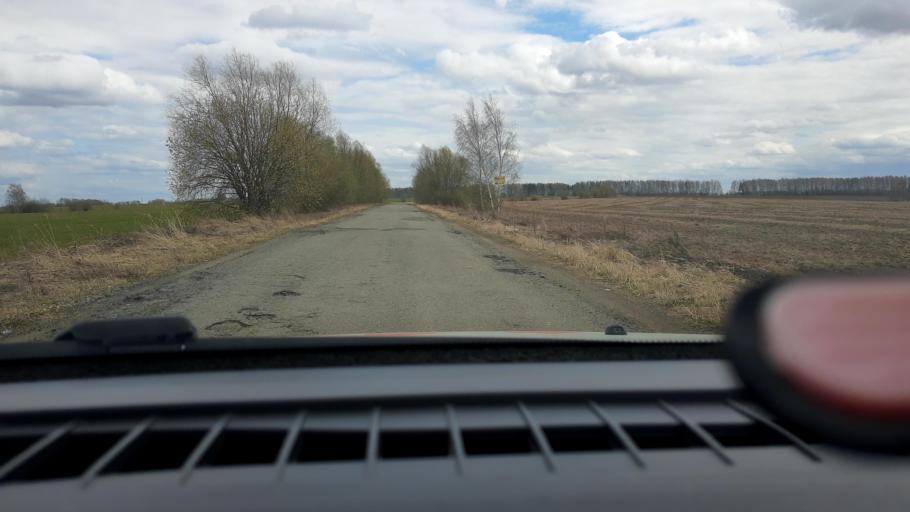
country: RU
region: Nizjnij Novgorod
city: Babino
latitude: 56.1622
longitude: 43.6912
